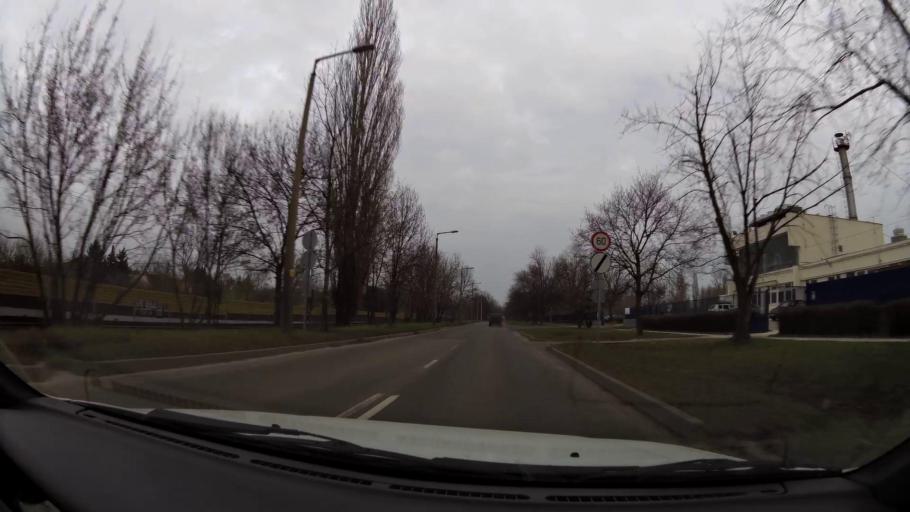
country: HU
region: Budapest
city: Budapest X. keruelet
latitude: 47.4819
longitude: 19.2046
